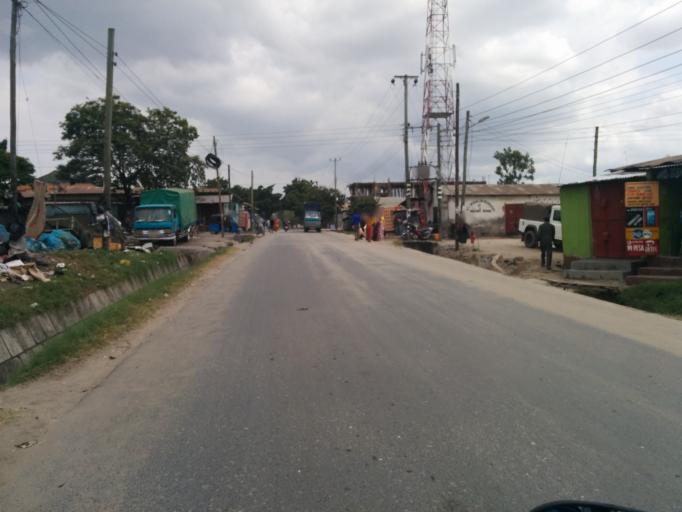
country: TZ
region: Dar es Salaam
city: Dar es Salaam
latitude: -6.8589
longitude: 39.2563
